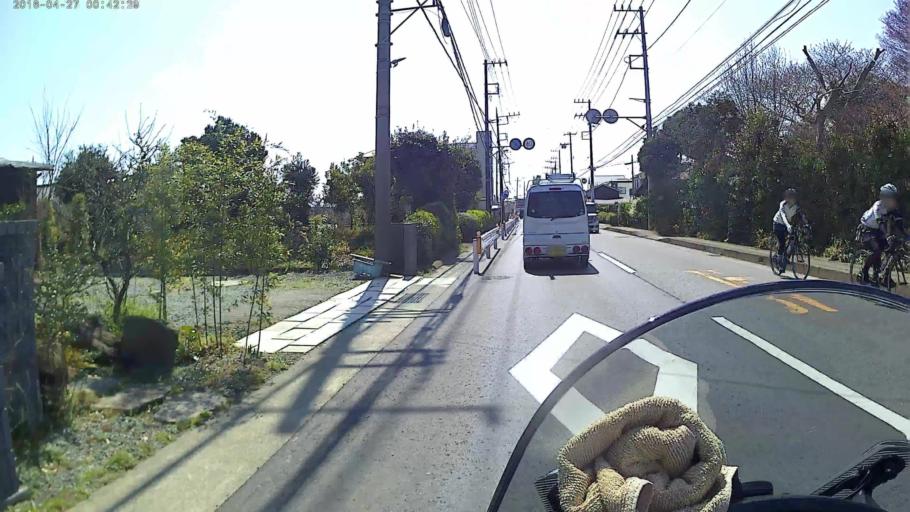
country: JP
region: Kanagawa
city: Atsugi
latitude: 35.3927
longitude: 139.4055
